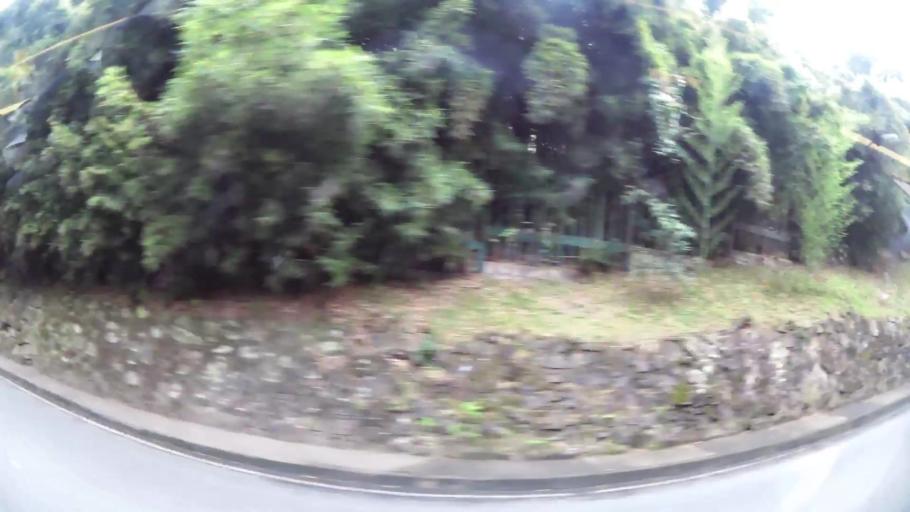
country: CO
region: Antioquia
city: Envigado
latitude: 6.1931
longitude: -75.5575
